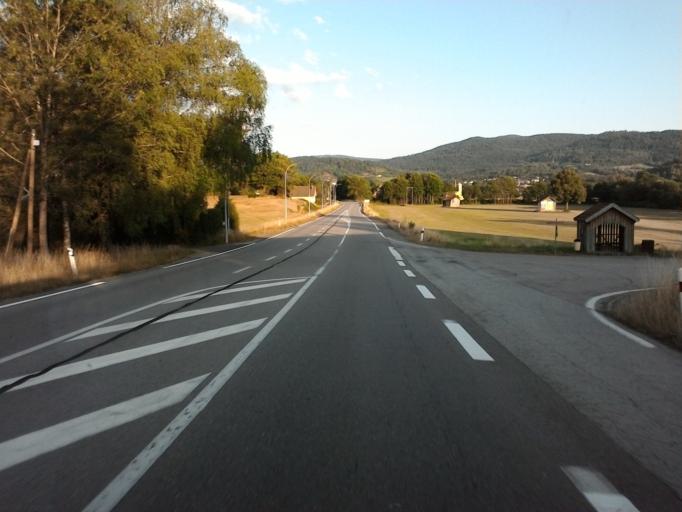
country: FR
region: Lorraine
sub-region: Departement des Vosges
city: Ramonchamp
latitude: 47.8896
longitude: 6.7490
